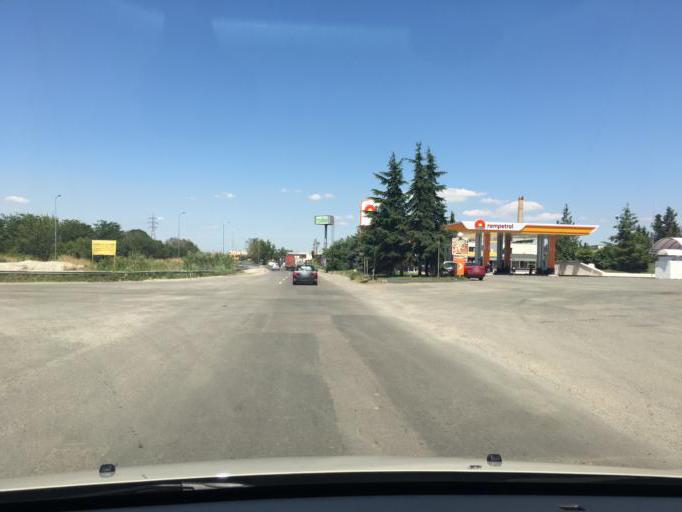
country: BG
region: Burgas
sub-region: Obshtina Burgas
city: Burgas
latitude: 42.4991
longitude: 27.4553
